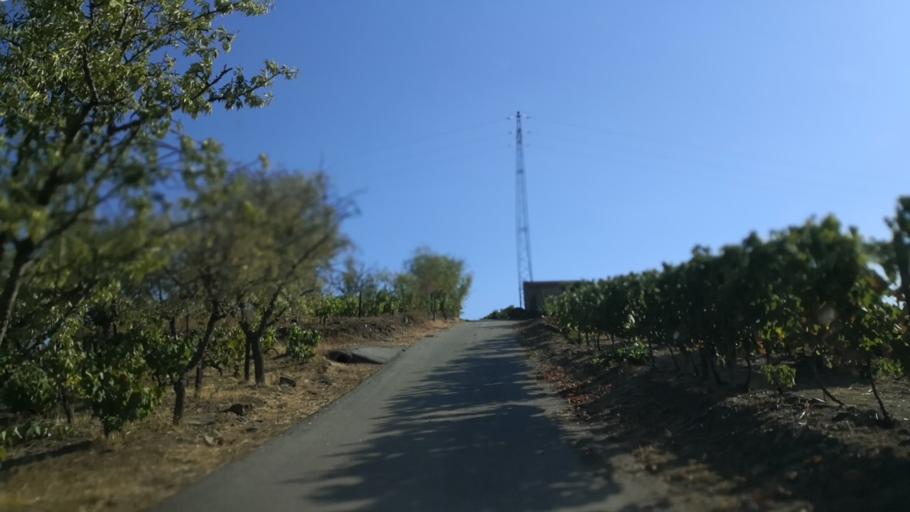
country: PT
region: Viseu
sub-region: Sao Joao da Pesqueira
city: Sao Joao da Pesqueira
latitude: 41.1857
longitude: -7.4004
